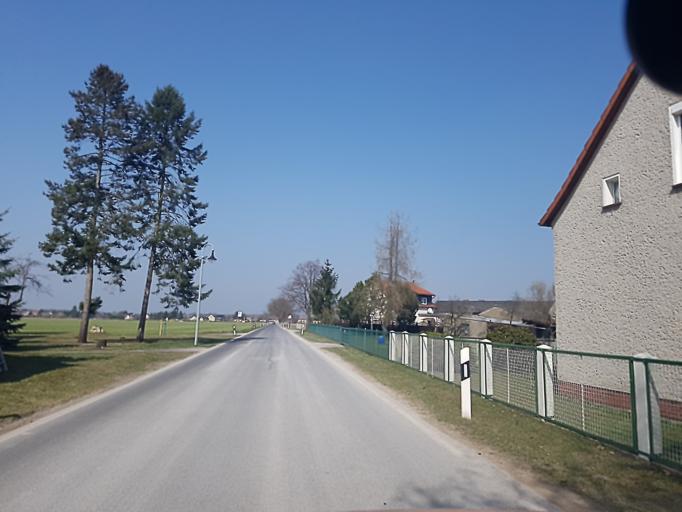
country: DE
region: Brandenburg
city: Forst
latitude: 51.6757
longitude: 14.5732
